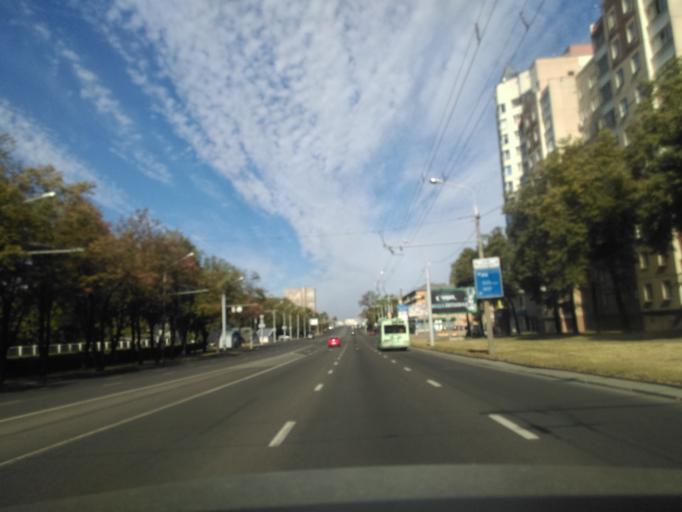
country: BY
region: Minsk
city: Minsk
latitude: 53.8828
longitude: 27.5946
